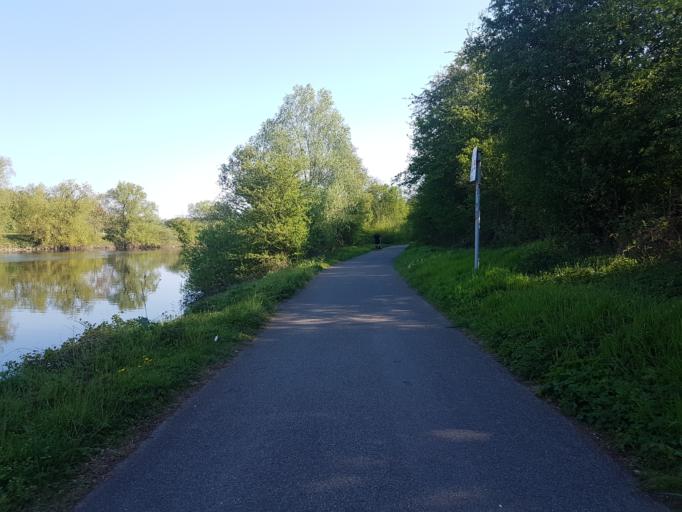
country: DE
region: North Rhine-Westphalia
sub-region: Regierungsbezirk Dusseldorf
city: Essen
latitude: 51.4399
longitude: 7.0836
